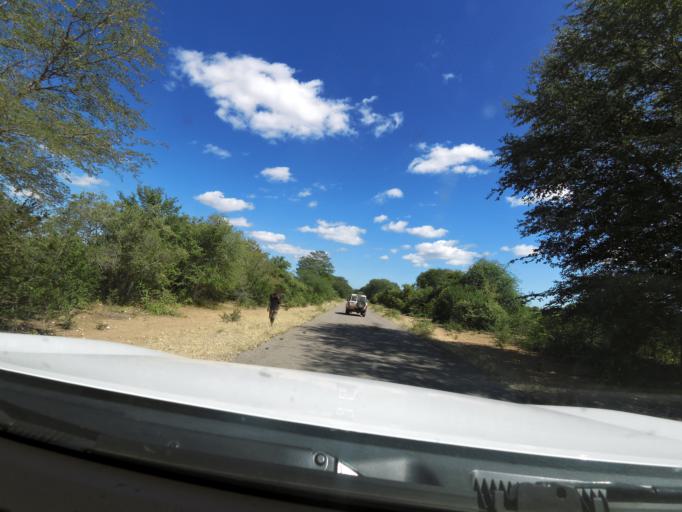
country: ZW
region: Matabeleland North
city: Kamativi Mine
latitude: -18.0062
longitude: 27.1535
